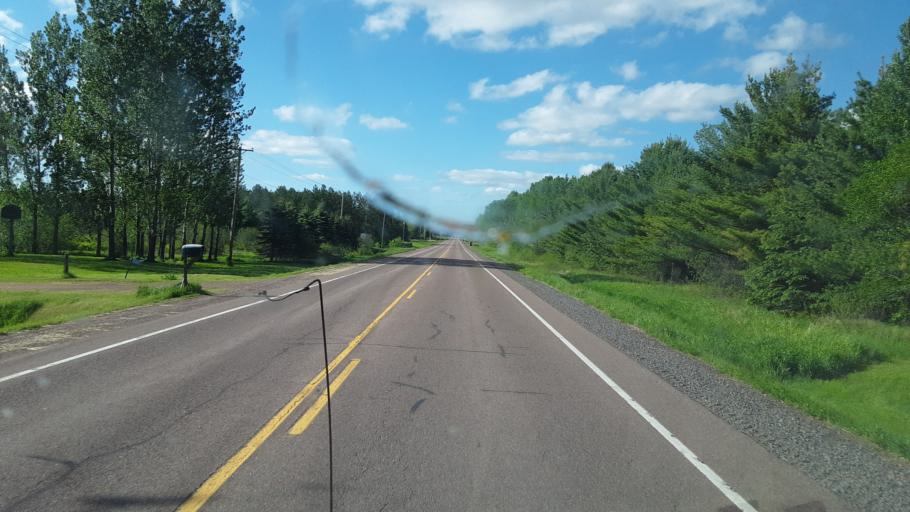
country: US
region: Wisconsin
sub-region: Wood County
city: Marshfield
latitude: 44.5605
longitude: -90.1805
